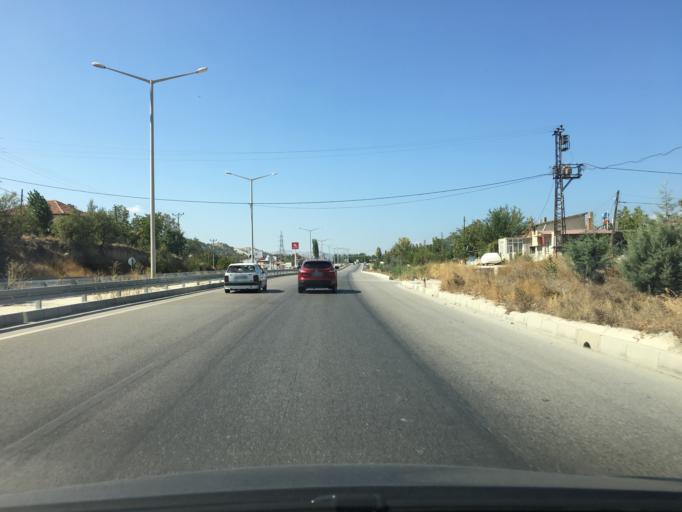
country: TR
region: Burdur
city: Burdur
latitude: 37.7580
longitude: 30.3418
